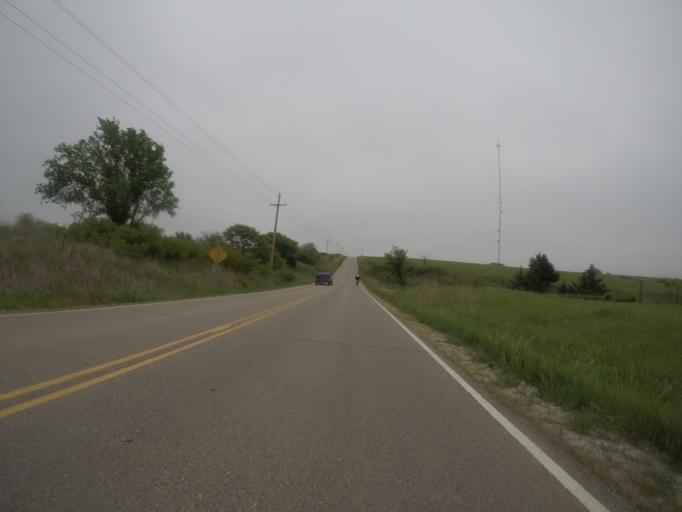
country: US
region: Kansas
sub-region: Pottawatomie County
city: Westmoreland
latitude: 39.5222
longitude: -96.3114
